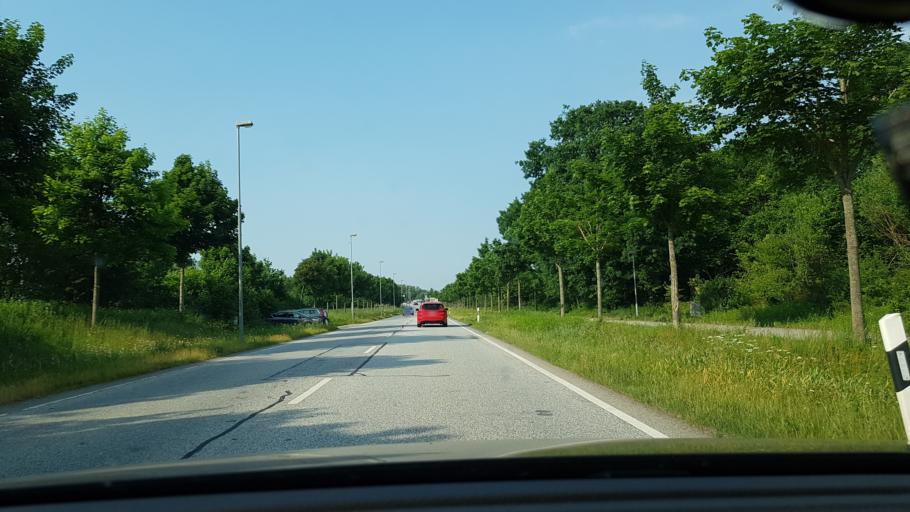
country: DE
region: Schleswig-Holstein
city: Luebeck
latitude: 53.8387
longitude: 10.6545
